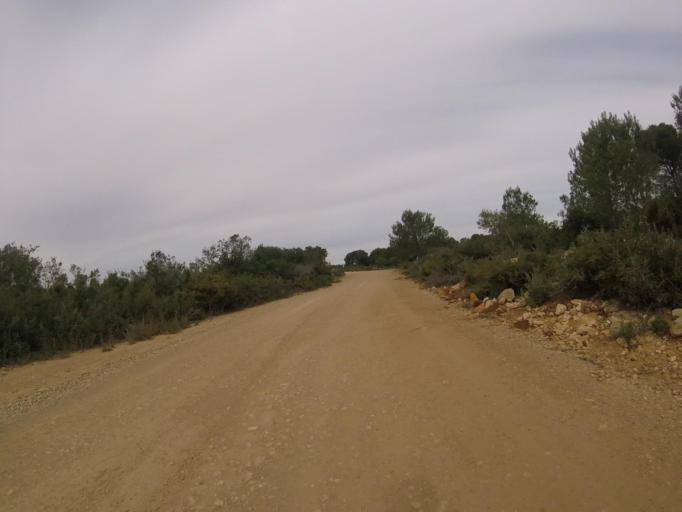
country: ES
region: Valencia
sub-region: Provincia de Castello
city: Benlloch
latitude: 40.1966
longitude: 0.0693
